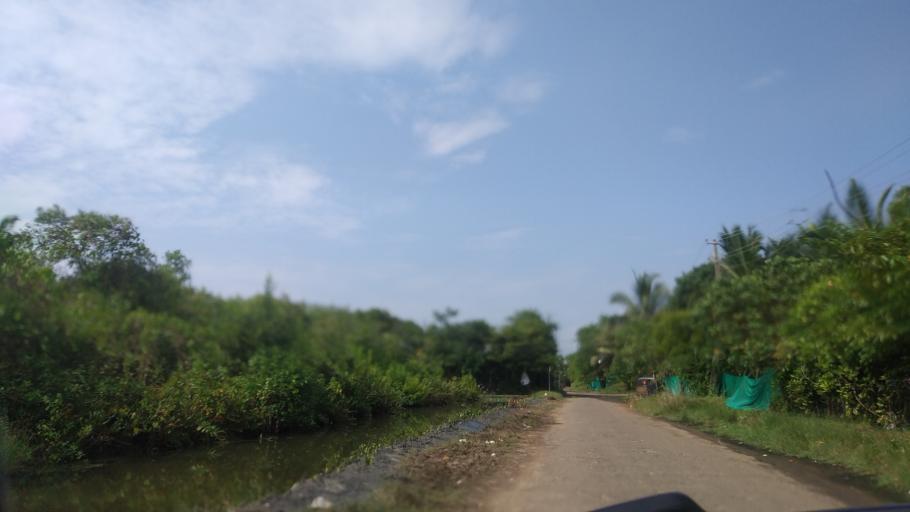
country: IN
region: Kerala
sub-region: Ernakulam
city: Elur
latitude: 10.0518
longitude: 76.2036
